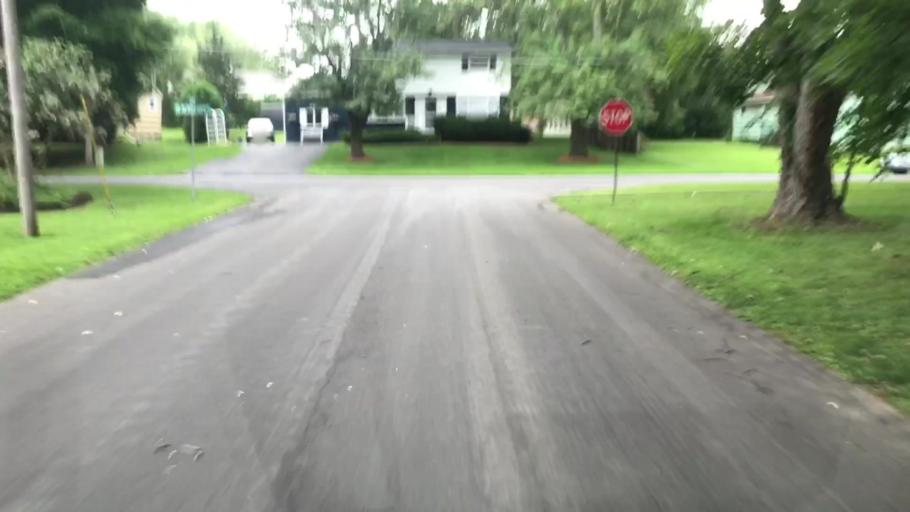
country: US
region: New York
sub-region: Onondaga County
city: Liverpool
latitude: 43.1389
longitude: -76.2161
